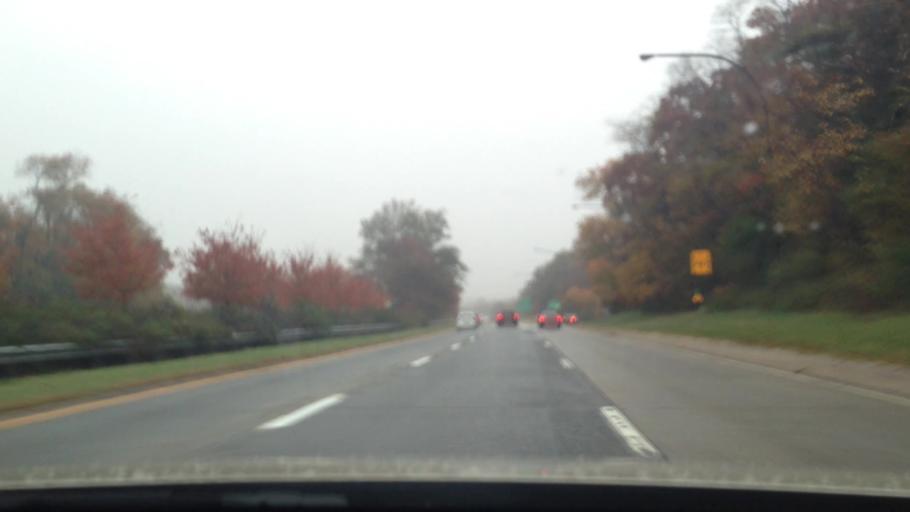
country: US
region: New York
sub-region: Suffolk County
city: Brentwood
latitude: 40.8004
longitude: -73.2792
